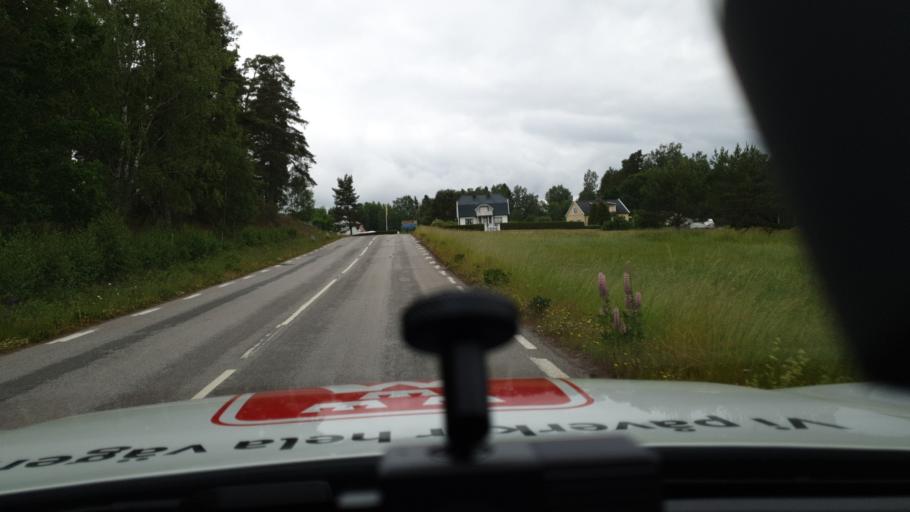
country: SE
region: Vaestra Goetaland
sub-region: Toreboda Kommun
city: Toereboda
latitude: 58.7864
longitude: 14.0845
